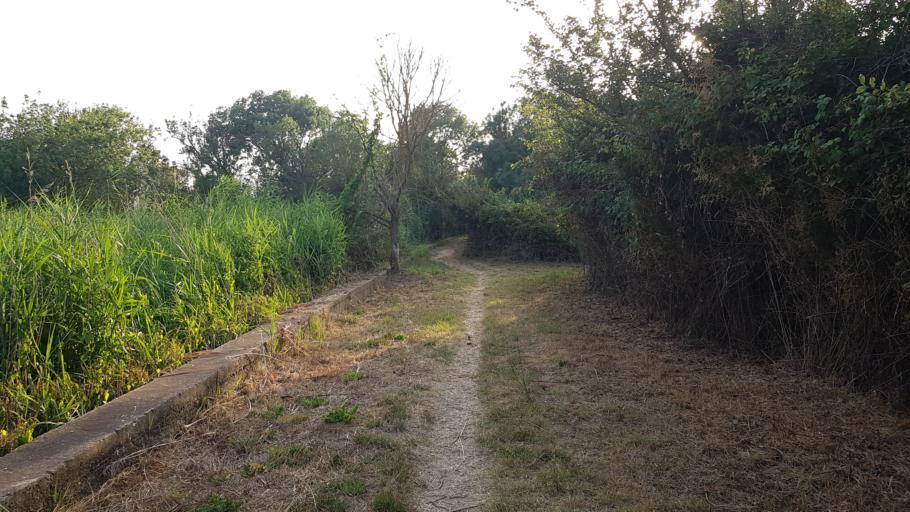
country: ES
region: Catalonia
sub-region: Provincia de Girona
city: Pals
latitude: 42.0067
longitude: 3.1929
